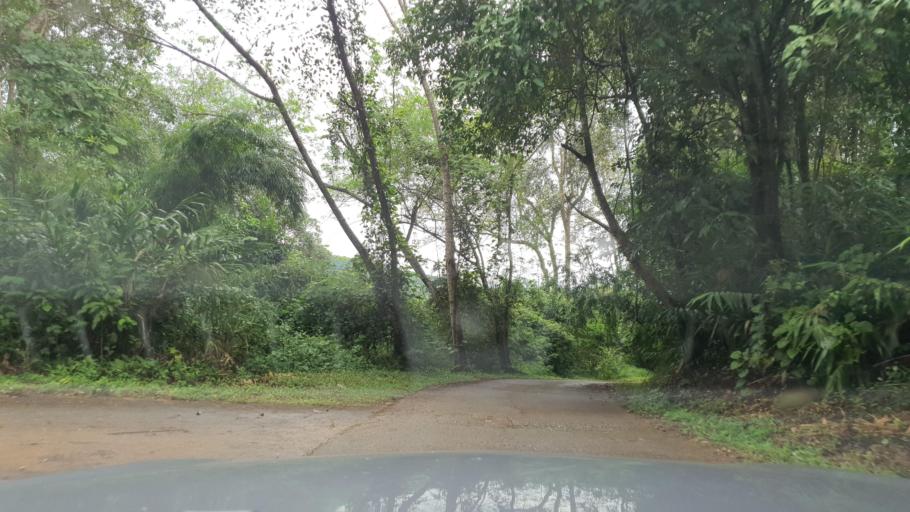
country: TH
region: Chiang Mai
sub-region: Amphoe Chiang Dao
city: Chiang Dao
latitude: 19.2767
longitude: 98.9594
